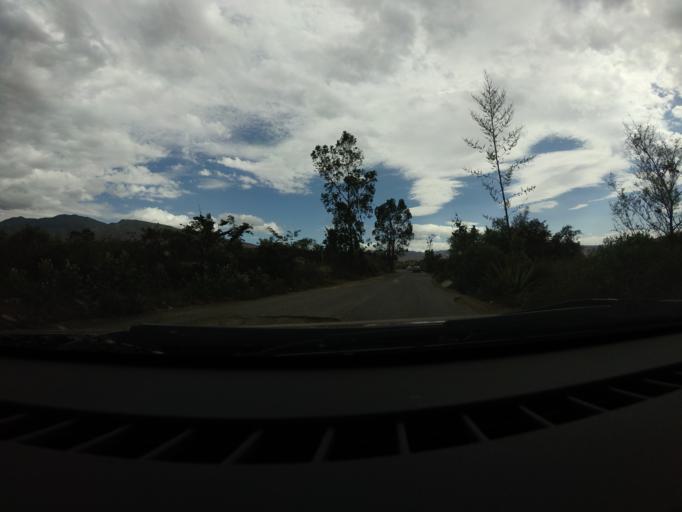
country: CO
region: Boyaca
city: Villa de Leiva
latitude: 5.6357
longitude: -73.5603
